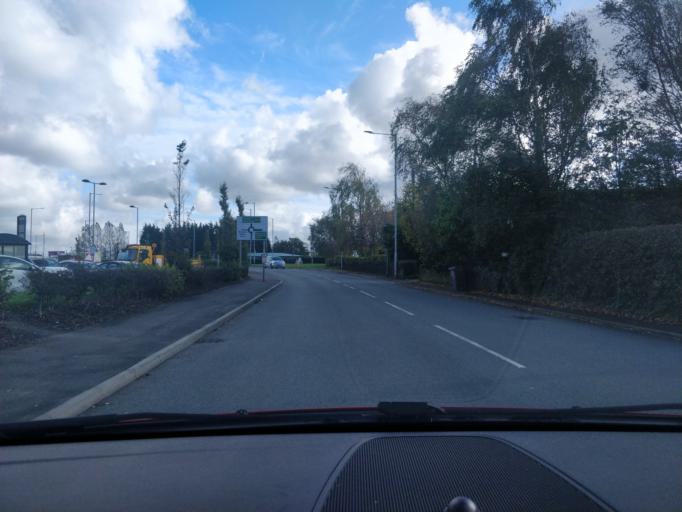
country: GB
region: England
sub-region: Lancashire
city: Ormskirk
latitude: 53.5874
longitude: -2.8654
